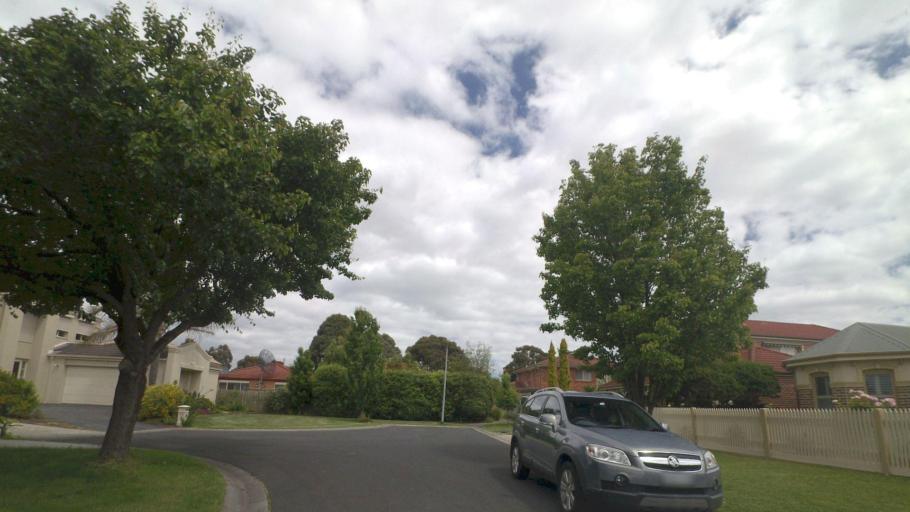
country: AU
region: Victoria
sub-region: Knox
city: Wantirna South
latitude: -37.8756
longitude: 145.2269
